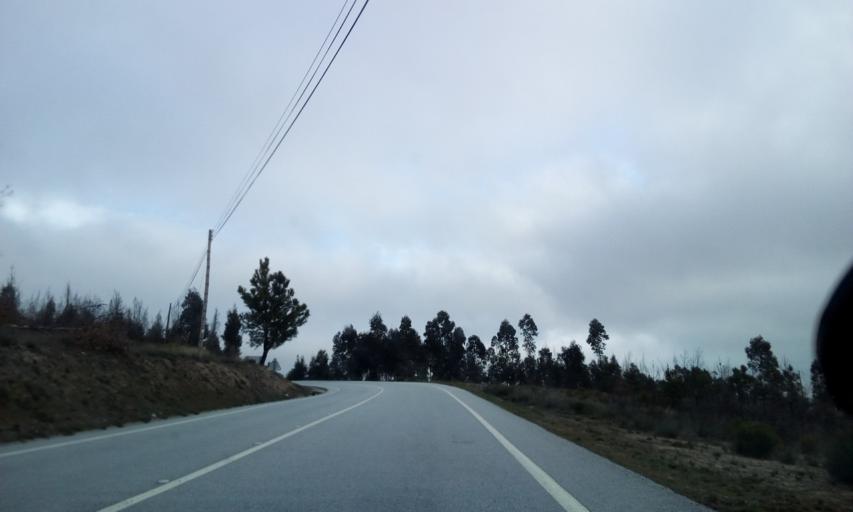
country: PT
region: Guarda
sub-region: Fornos de Algodres
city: Fornos de Algodres
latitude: 40.6654
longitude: -7.4752
